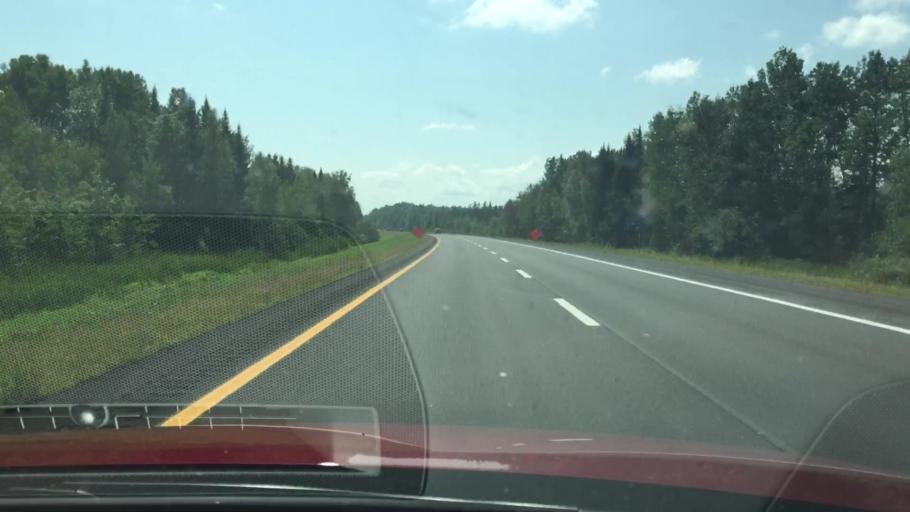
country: US
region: Maine
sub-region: Penobscot County
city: Patten
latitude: 45.8881
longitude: -68.4058
